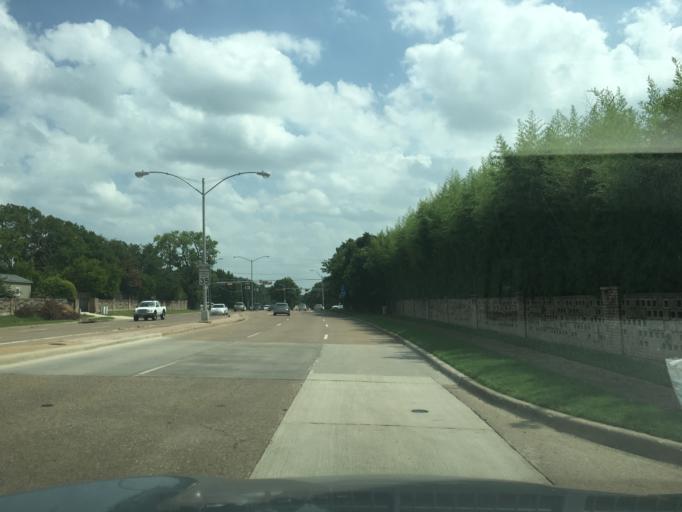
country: US
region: Texas
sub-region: Dallas County
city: University Park
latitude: 32.8964
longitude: -96.8199
